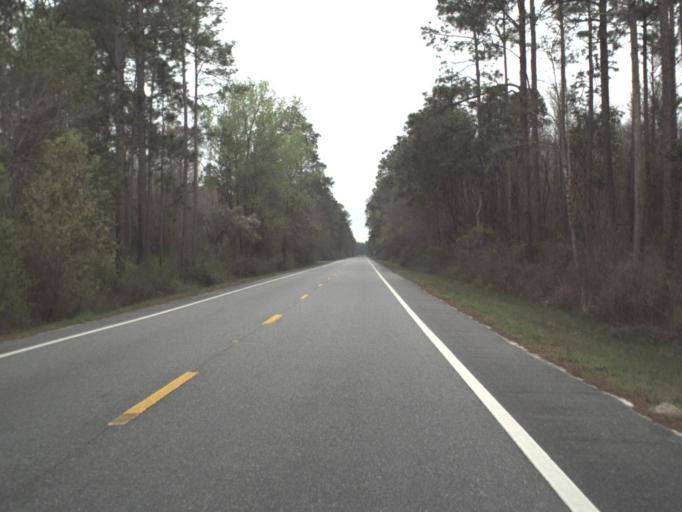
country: US
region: Florida
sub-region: Franklin County
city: Apalachicola
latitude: 29.9106
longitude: -84.9776
